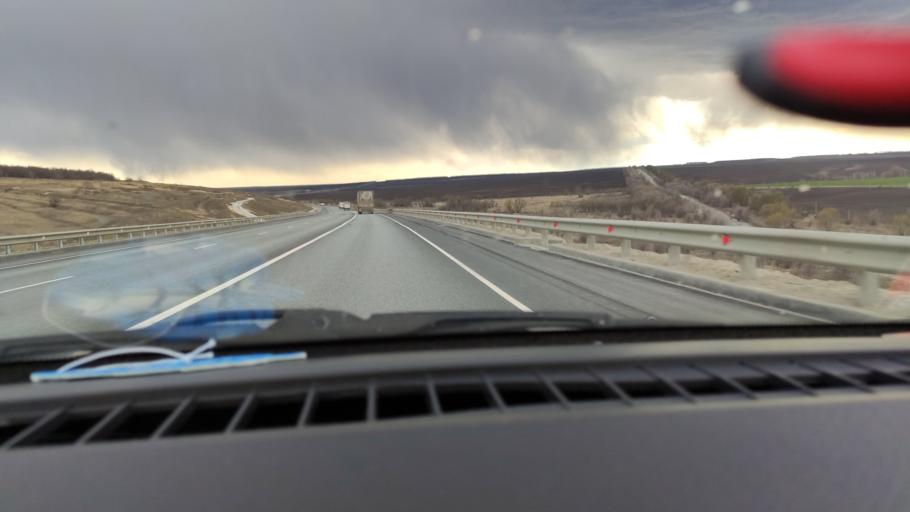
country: RU
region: Saratov
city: Yelshanka
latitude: 51.8750
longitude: 46.5062
